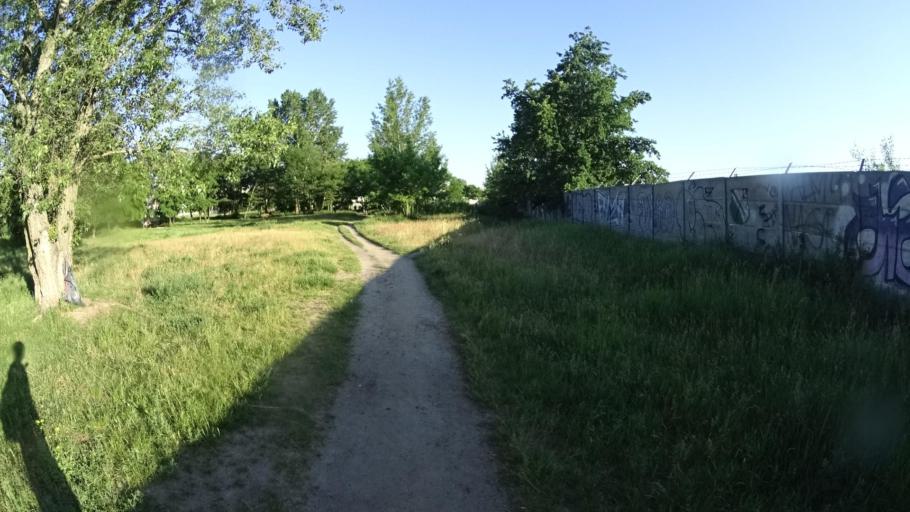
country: PL
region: Masovian Voivodeship
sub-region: Warszawa
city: Bemowo
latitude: 52.2609
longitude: 20.9139
